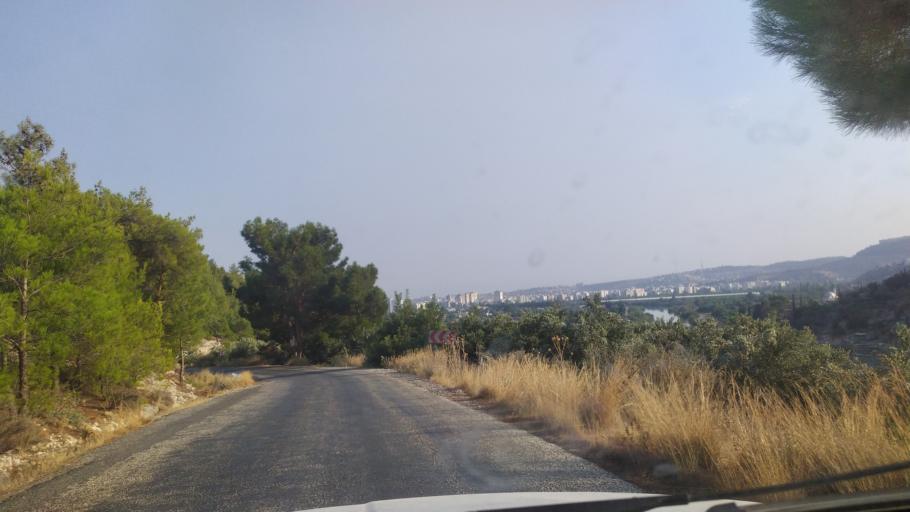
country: TR
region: Mersin
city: Silifke
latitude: 36.4055
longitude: 33.9232
